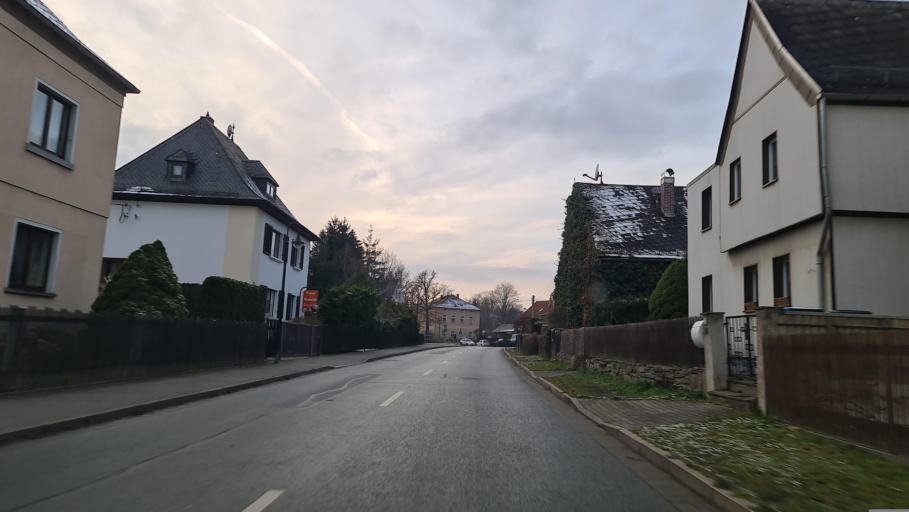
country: DE
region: Saxony
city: Limbach
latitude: 50.5827
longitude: 12.2502
